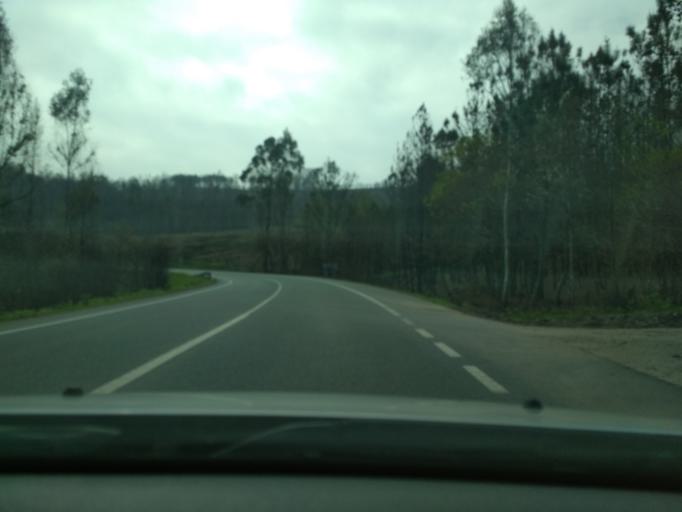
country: ES
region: Galicia
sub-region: Provincia de Pontevedra
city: Catoira
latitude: 42.6523
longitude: -8.6900
